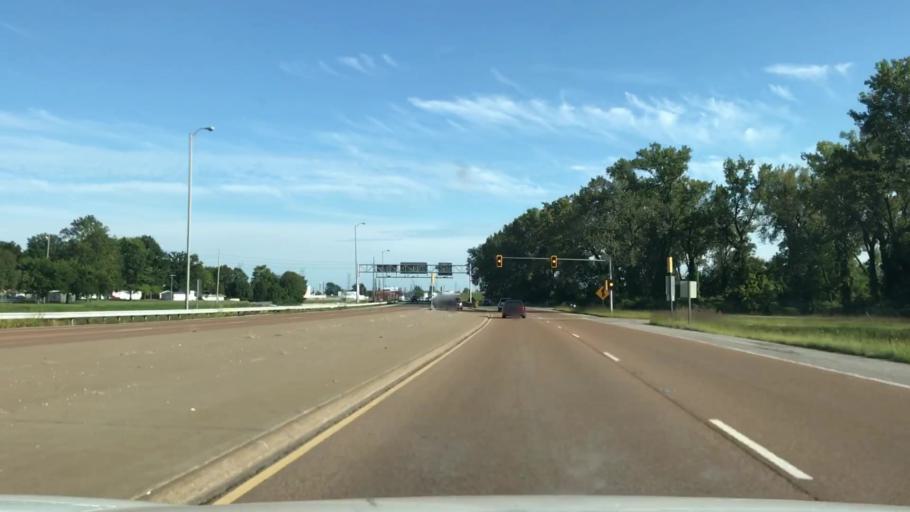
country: US
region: Illinois
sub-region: Madison County
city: Wood River
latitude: 38.8578
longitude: -90.1086
